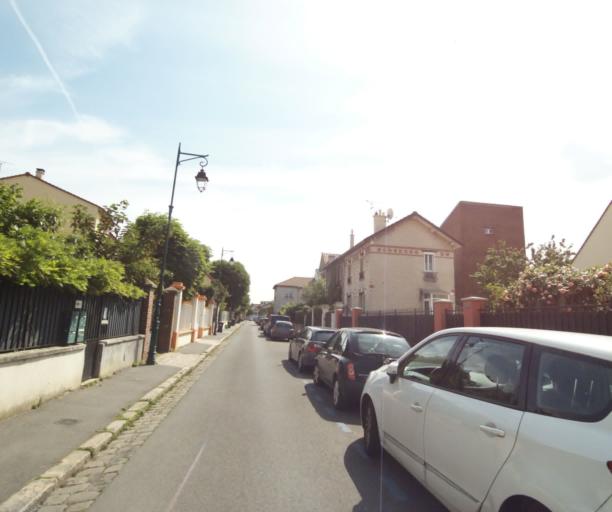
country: FR
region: Ile-de-France
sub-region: Departement des Hauts-de-Seine
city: La Garenne-Colombes
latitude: 48.9133
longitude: 2.2414
